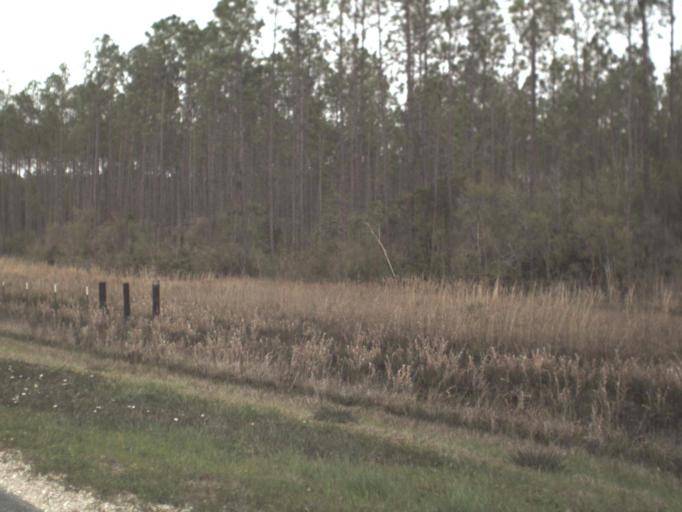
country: US
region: Florida
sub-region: Leon County
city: Woodville
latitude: 30.1963
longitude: -84.1497
